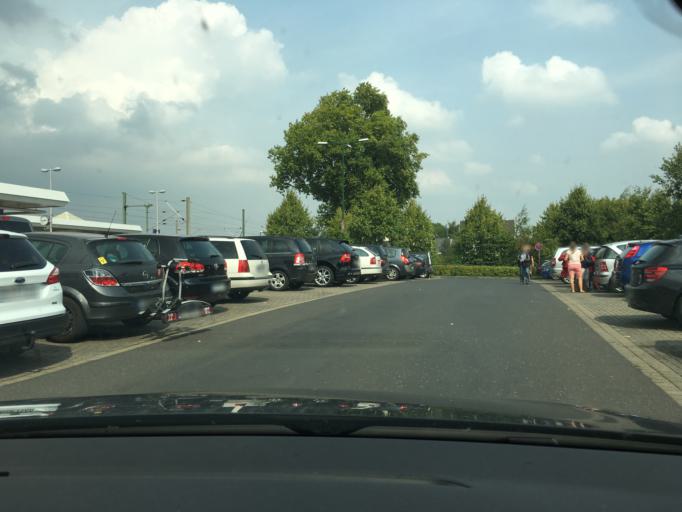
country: DE
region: North Rhine-Westphalia
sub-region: Regierungsbezirk Koln
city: Merzenich
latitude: 50.8622
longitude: 6.5750
